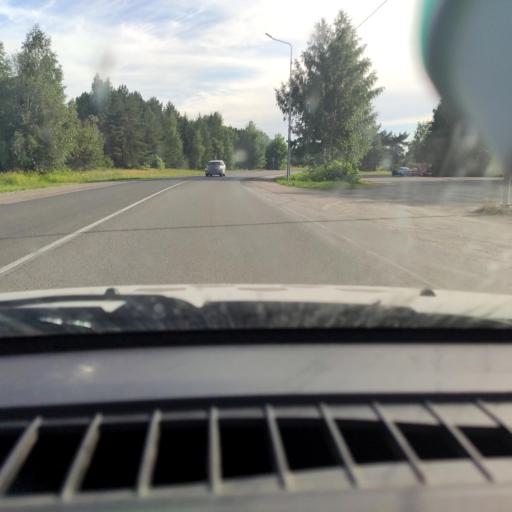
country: RU
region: Kirov
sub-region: Kirovo-Chepetskiy Rayon
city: Kirov
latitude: 58.6200
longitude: 49.7748
